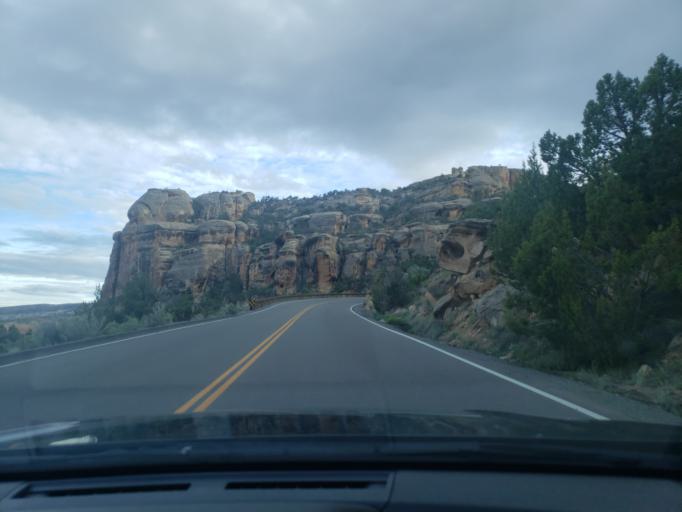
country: US
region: Colorado
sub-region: Mesa County
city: Redlands
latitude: 39.0304
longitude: -108.6460
